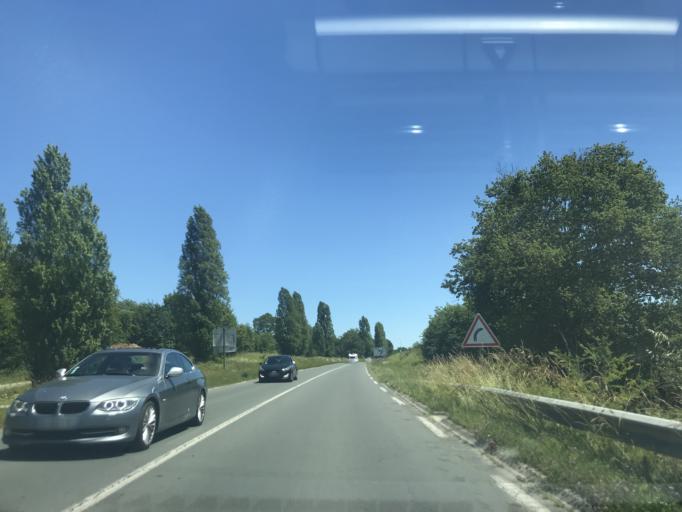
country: FR
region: Poitou-Charentes
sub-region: Departement de la Charente-Maritime
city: Vaux-sur-Mer
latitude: 45.6633
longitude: -1.0656
